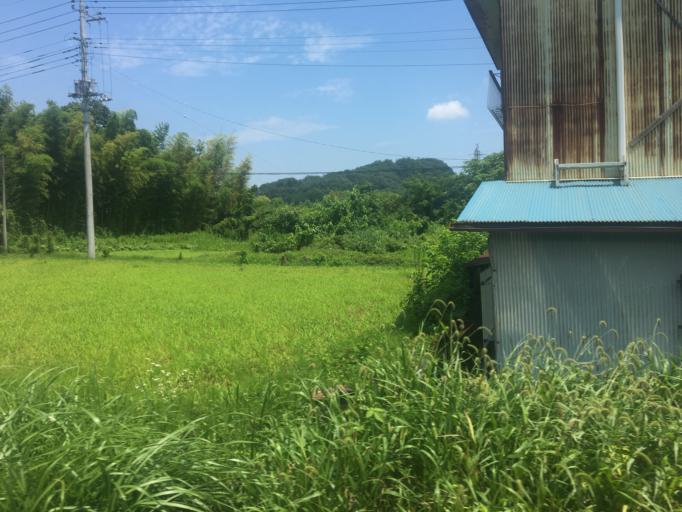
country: JP
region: Saitama
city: Yorii
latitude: 36.0991
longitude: 139.1932
